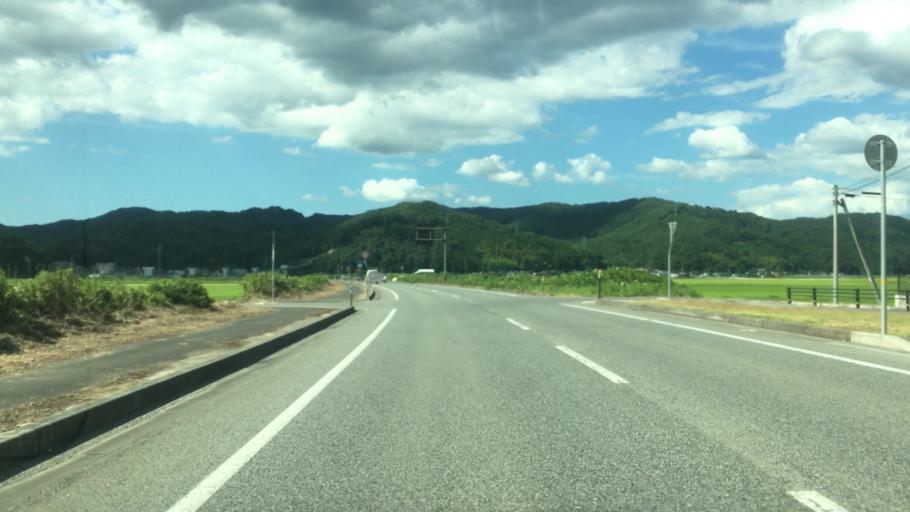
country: JP
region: Hyogo
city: Toyooka
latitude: 35.4838
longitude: 134.7853
